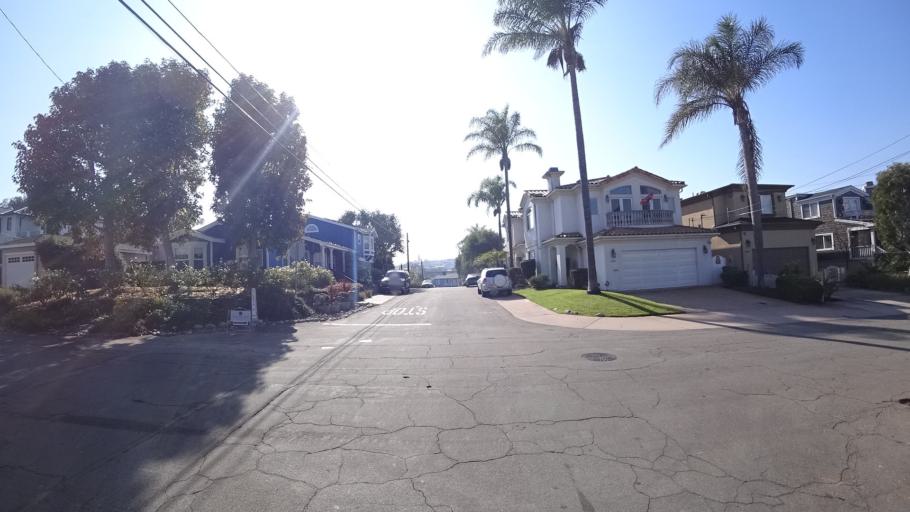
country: US
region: California
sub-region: Los Angeles County
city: Manhattan Beach
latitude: 33.8955
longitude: -118.4072
